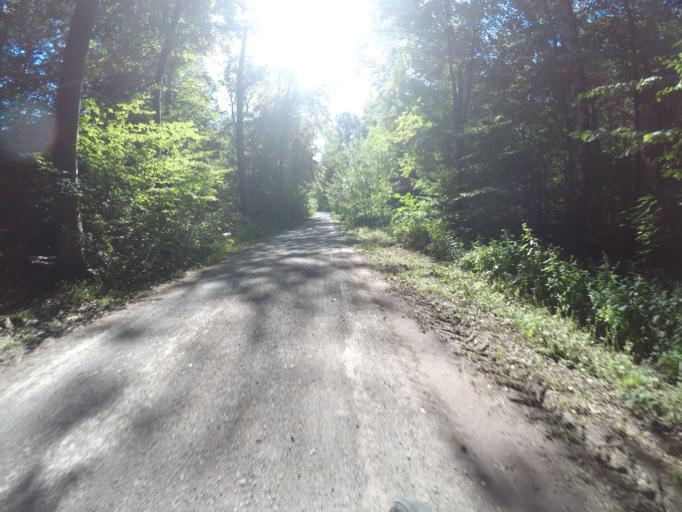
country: DE
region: Baden-Wuerttemberg
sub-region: Regierungsbezirk Stuttgart
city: Gerlingen
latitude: 48.7706
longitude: 9.1096
